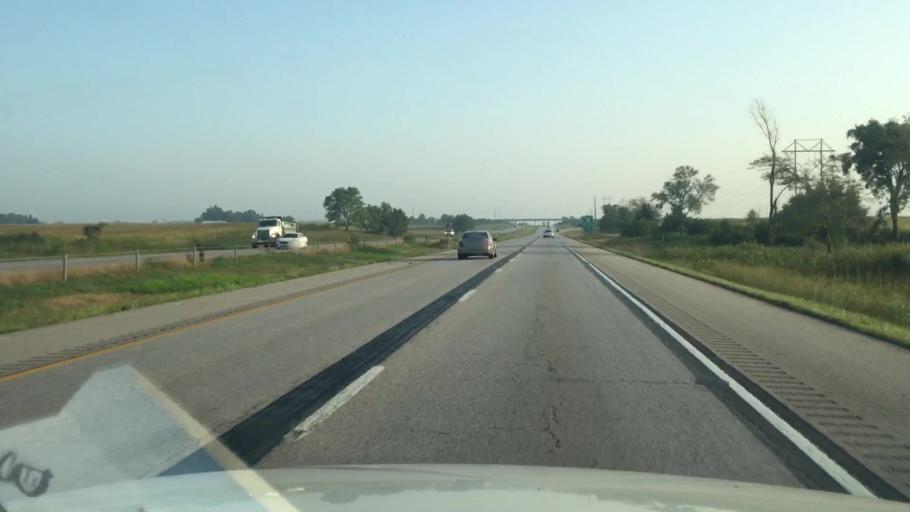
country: US
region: Iowa
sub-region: Story County
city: Huxley
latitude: 41.8690
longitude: -93.5711
